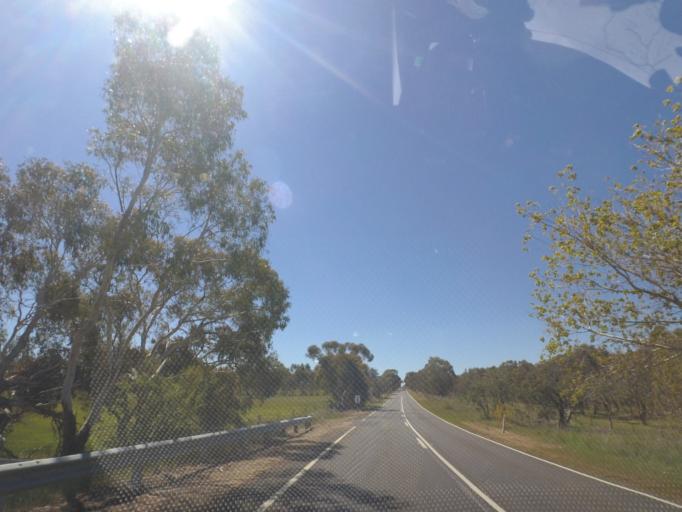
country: AU
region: Victoria
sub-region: Hume
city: Sunbury
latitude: -37.1315
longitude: 144.7672
